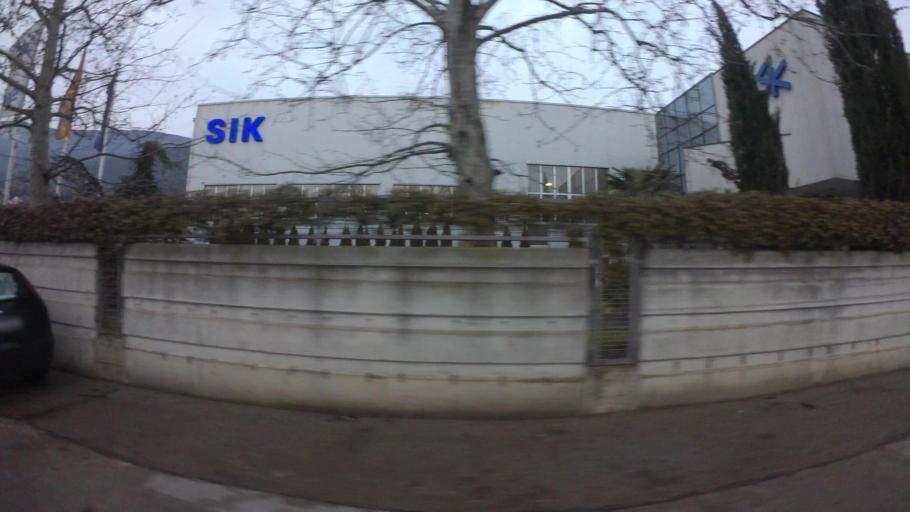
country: BA
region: Federation of Bosnia and Herzegovina
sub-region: Hercegovacko-Bosanski Kanton
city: Mostar
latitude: 43.3668
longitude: 17.8106
